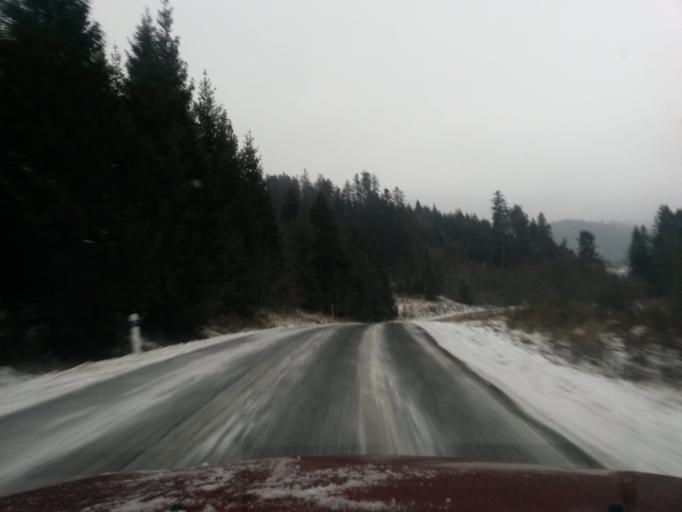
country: SK
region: Kosicky
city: Medzev
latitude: 48.7221
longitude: 20.7120
